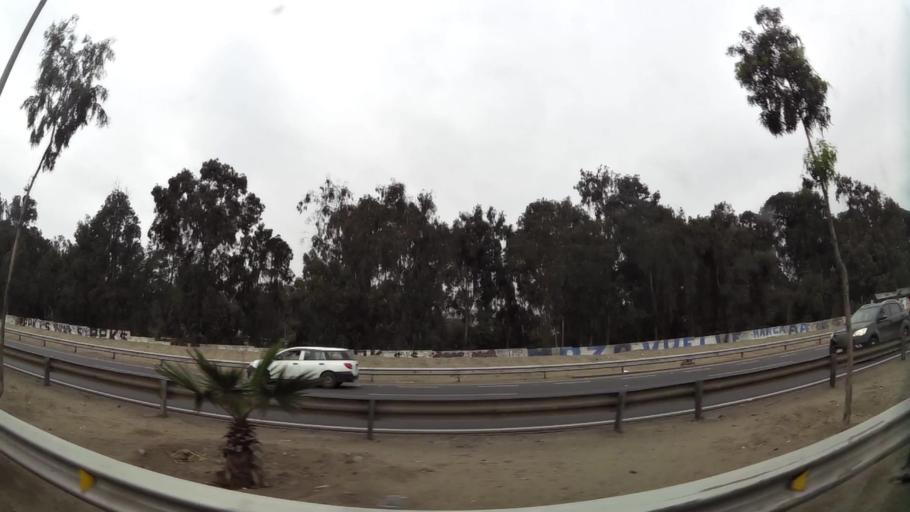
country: PE
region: Lima
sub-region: Lima
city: Surco
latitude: -12.1835
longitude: -76.9752
